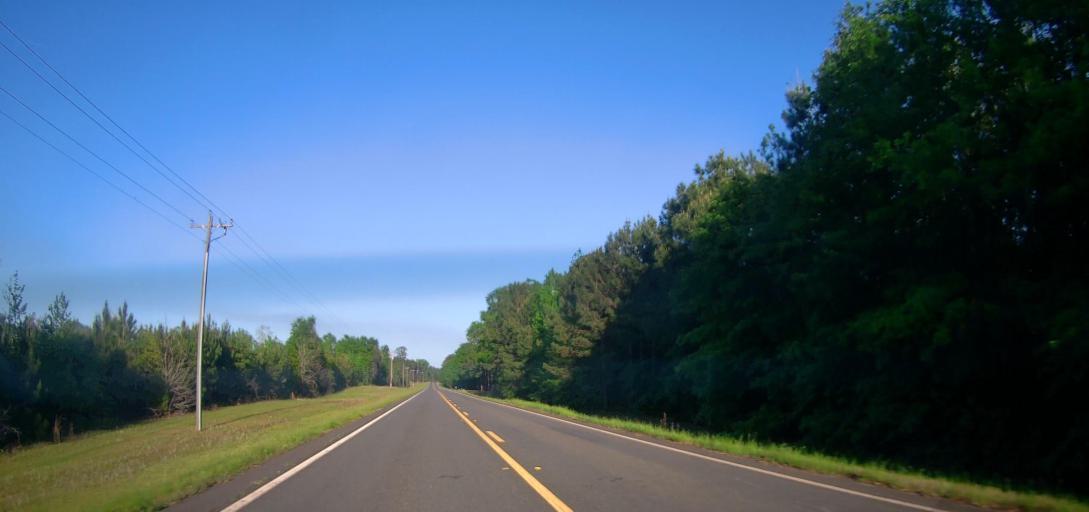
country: US
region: Georgia
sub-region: Schley County
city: Ellaville
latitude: 32.3213
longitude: -84.2134
